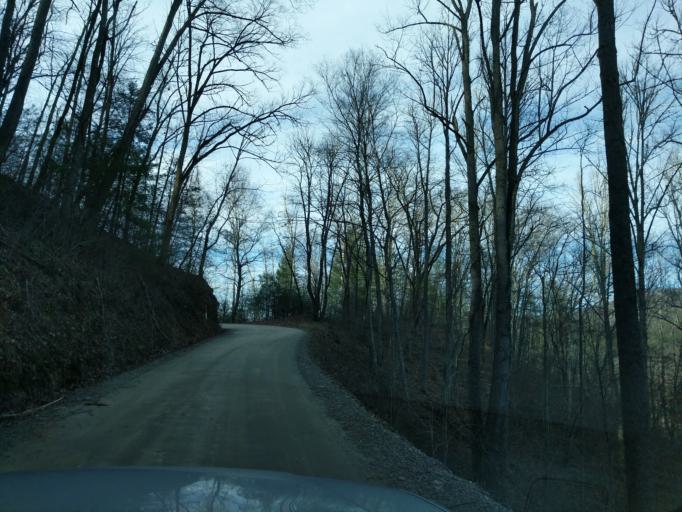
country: US
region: North Carolina
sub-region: Haywood County
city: Cove Creek
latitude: 35.6696
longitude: -83.0234
